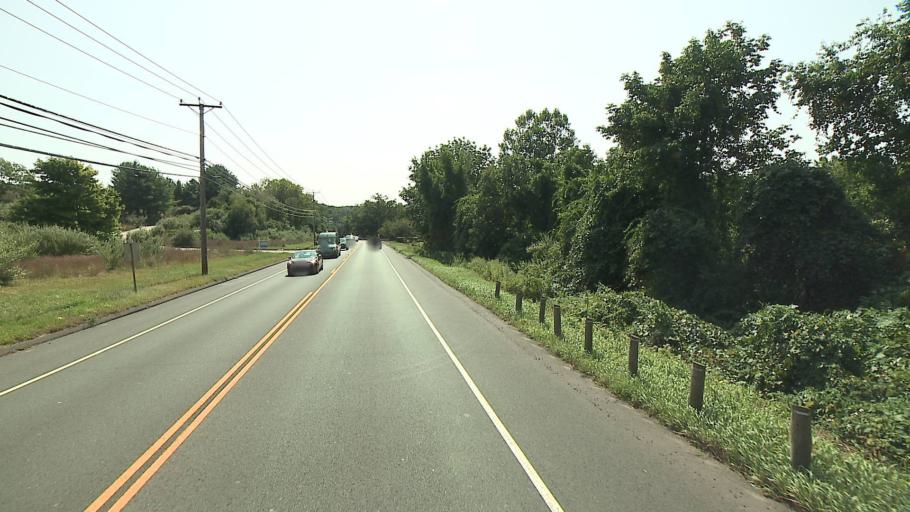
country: US
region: Connecticut
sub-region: Fairfield County
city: Newtown
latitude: 41.3780
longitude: -73.2777
